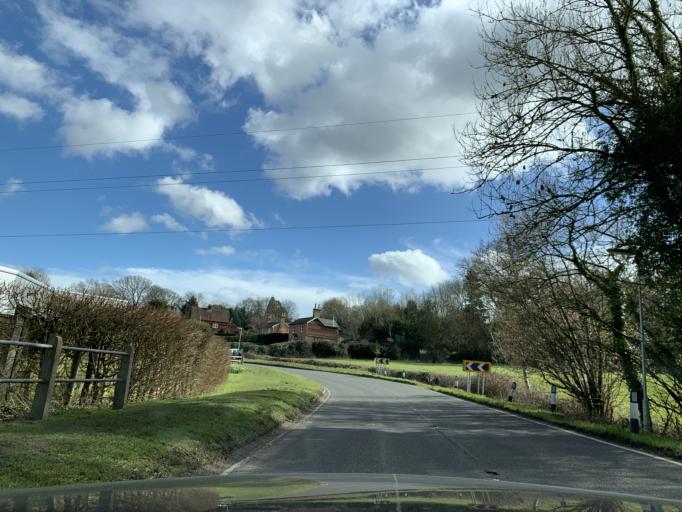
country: GB
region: England
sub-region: West Sussex
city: Crawley Down
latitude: 51.1086
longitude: -0.0899
